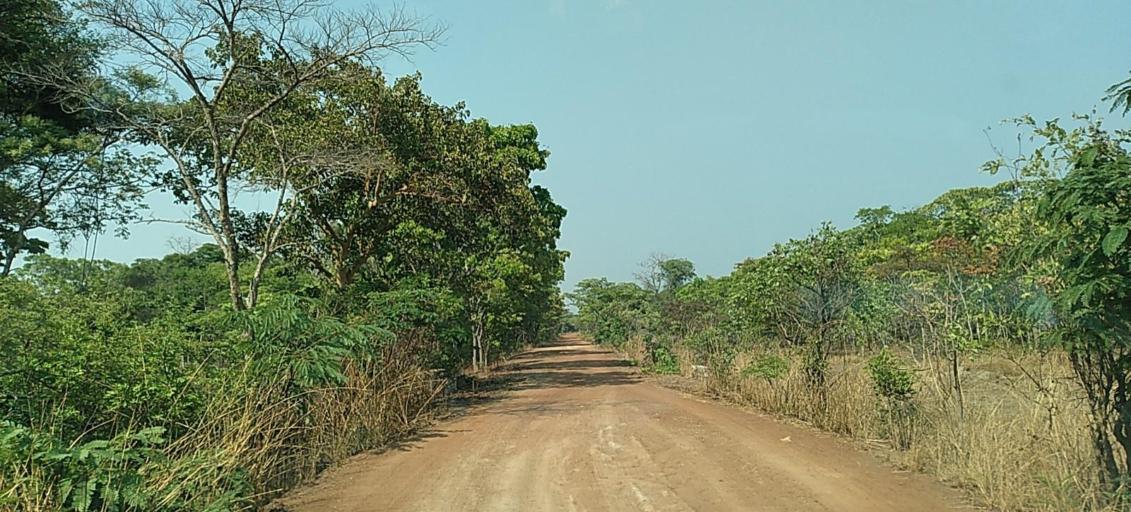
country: ZM
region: Copperbelt
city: Chingola
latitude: -12.8760
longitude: 27.4471
